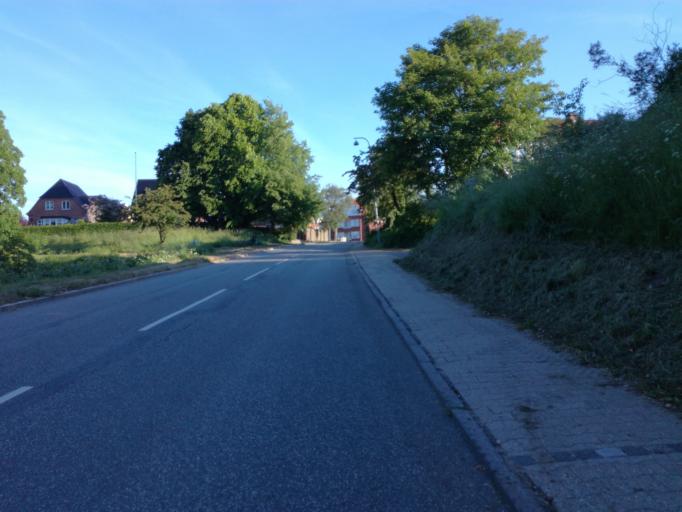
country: DK
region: South Denmark
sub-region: Fredericia Kommune
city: Fredericia
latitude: 55.5718
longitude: 9.7668
